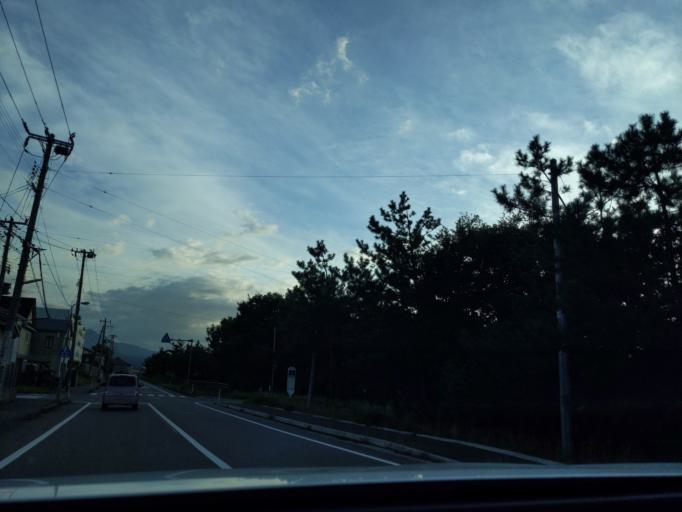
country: JP
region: Niigata
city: Kashiwazaki
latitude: 37.3793
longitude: 138.5577
